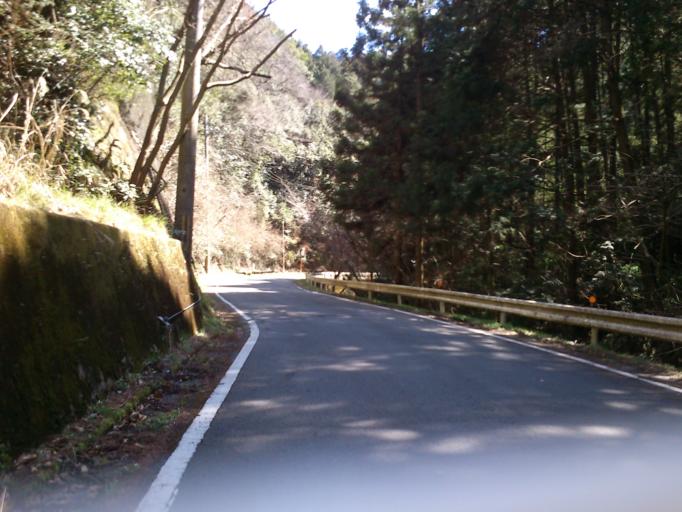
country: JP
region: Kyoto
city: Uji
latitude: 34.8295
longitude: 135.8788
